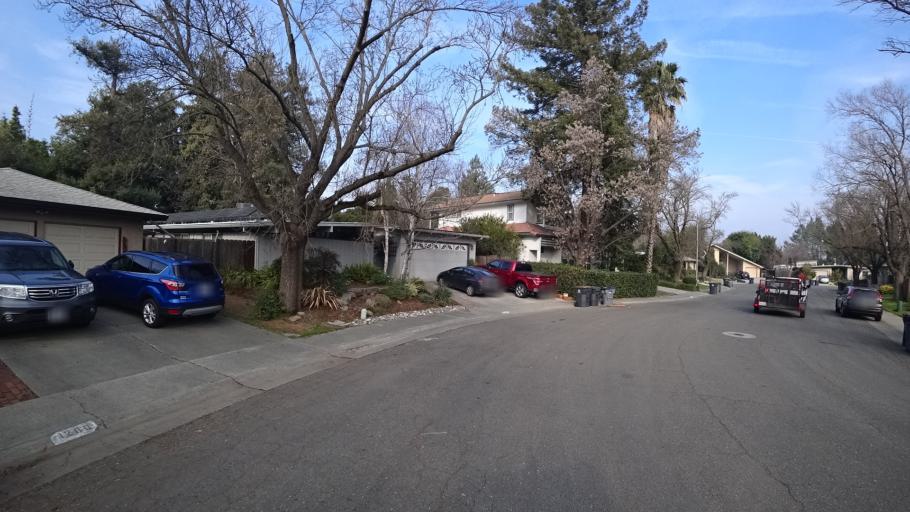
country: US
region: California
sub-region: Yolo County
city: Davis
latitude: 38.5571
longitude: -121.7639
